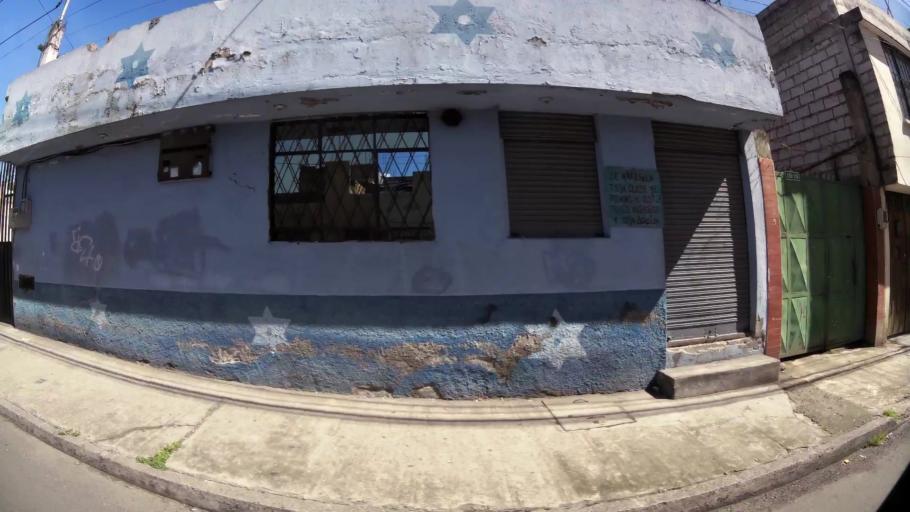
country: EC
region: Pichincha
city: Quito
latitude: -0.2823
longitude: -78.5590
